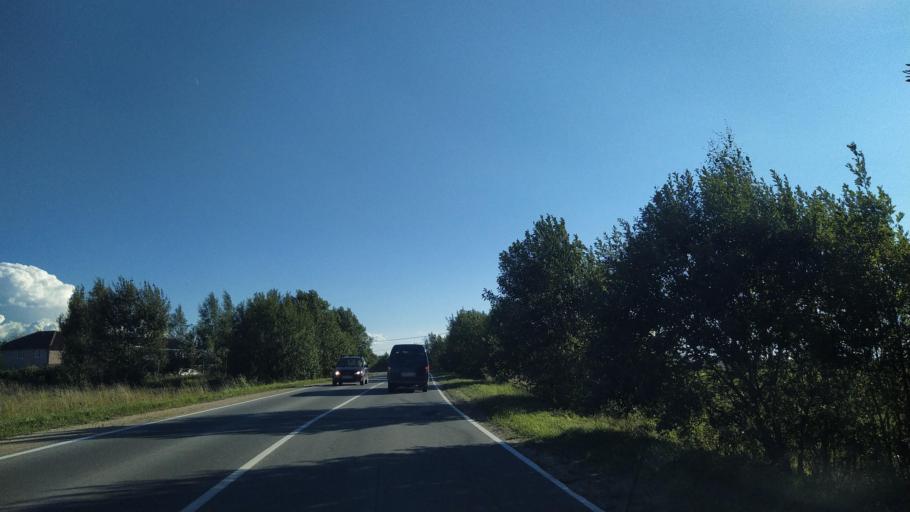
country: RU
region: Leningrad
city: Siverskiy
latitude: 59.3334
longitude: 30.0311
